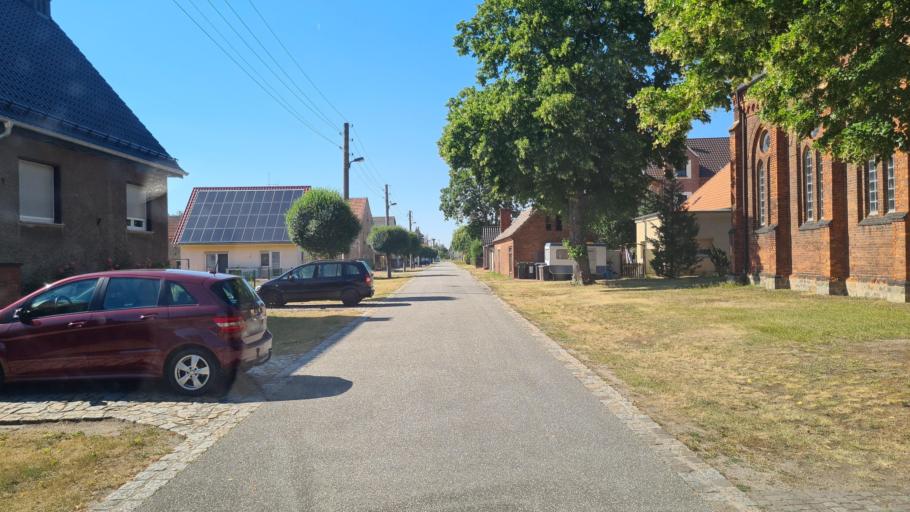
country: DE
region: Saxony-Anhalt
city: Annaburg
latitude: 51.6967
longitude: 12.9952
